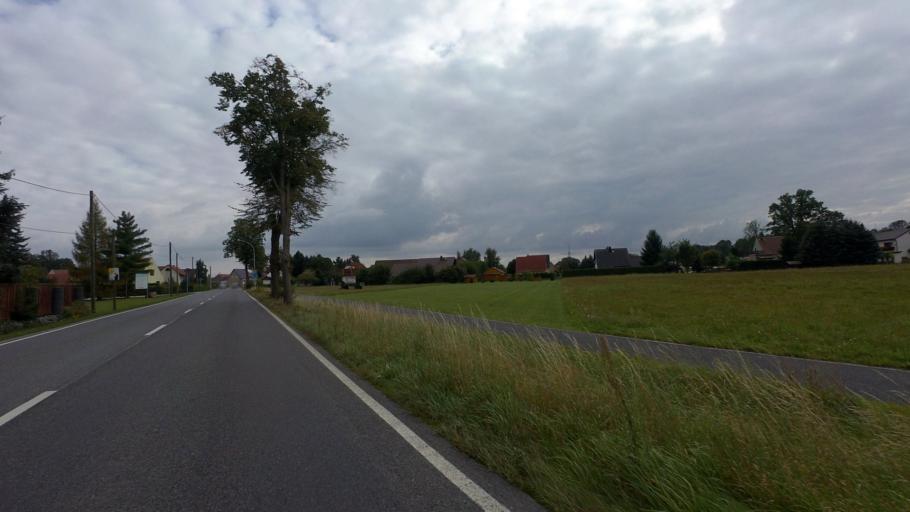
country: DE
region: Saxony
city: Konigswartha
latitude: 51.3530
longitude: 14.3246
